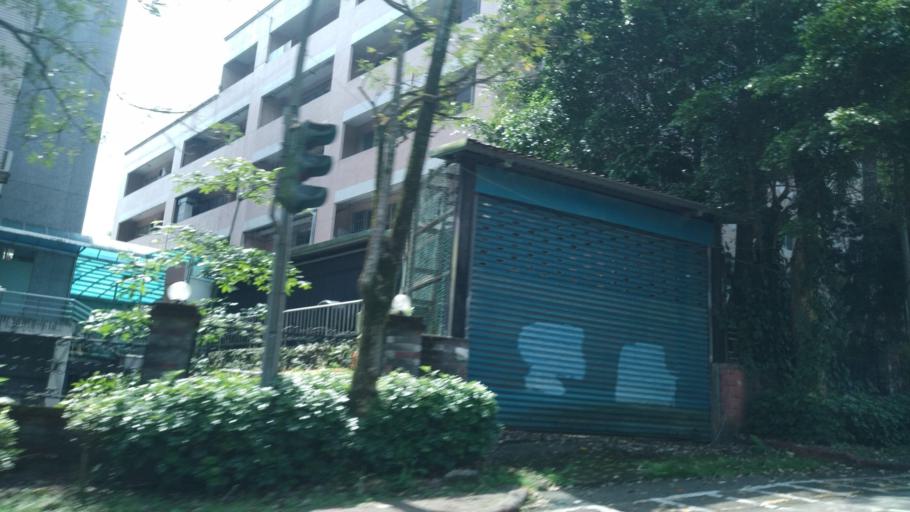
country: TW
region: Taipei
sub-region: Taipei
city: Banqiao
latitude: 24.9526
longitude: 121.5088
